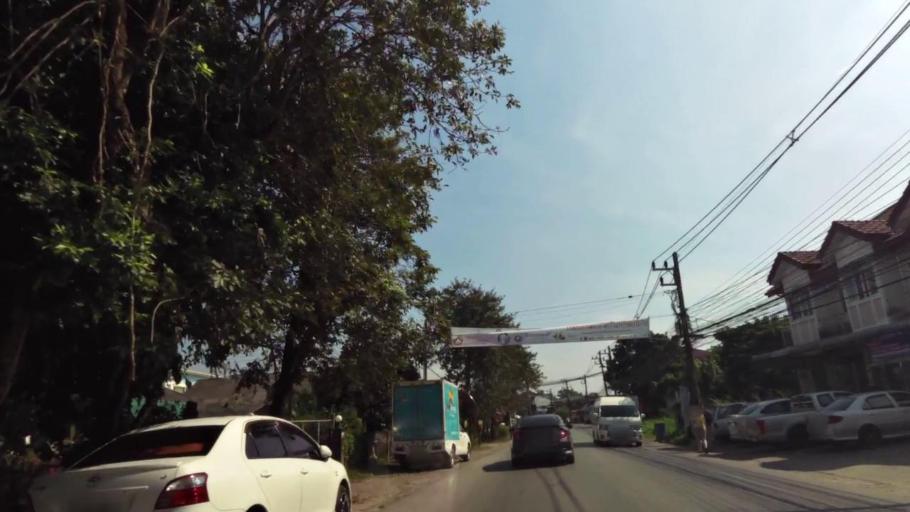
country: TH
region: Chiang Rai
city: Chiang Rai
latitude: 19.9257
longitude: 99.8374
